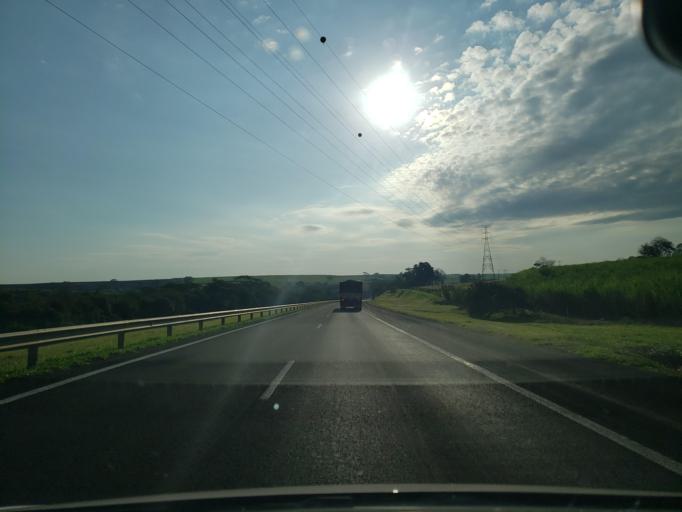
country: BR
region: Sao Paulo
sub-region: Valparaiso
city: Valparaiso
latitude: -21.2031
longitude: -50.8919
